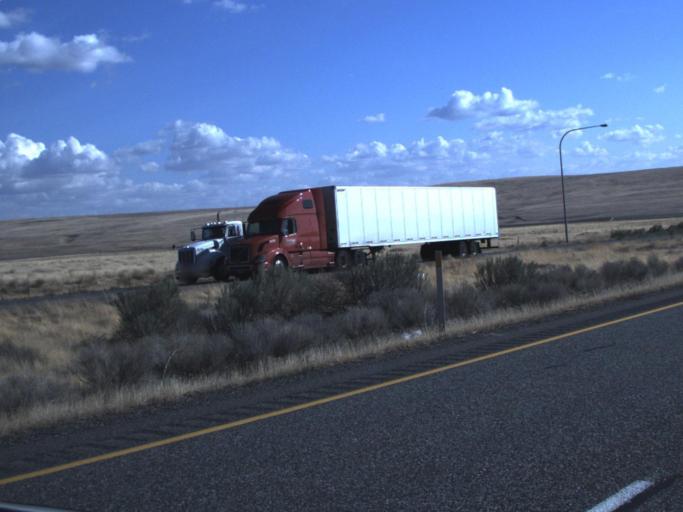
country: US
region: Washington
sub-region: Benton County
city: Highland
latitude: 46.0327
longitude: -119.2249
